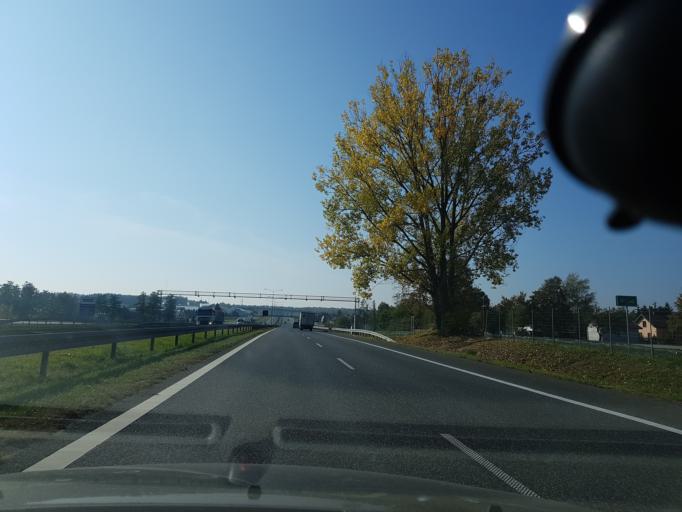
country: PL
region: Masovian Voivodeship
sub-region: Powiat zyrardowski
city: Mszczonow
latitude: 51.9443
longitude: 20.4844
